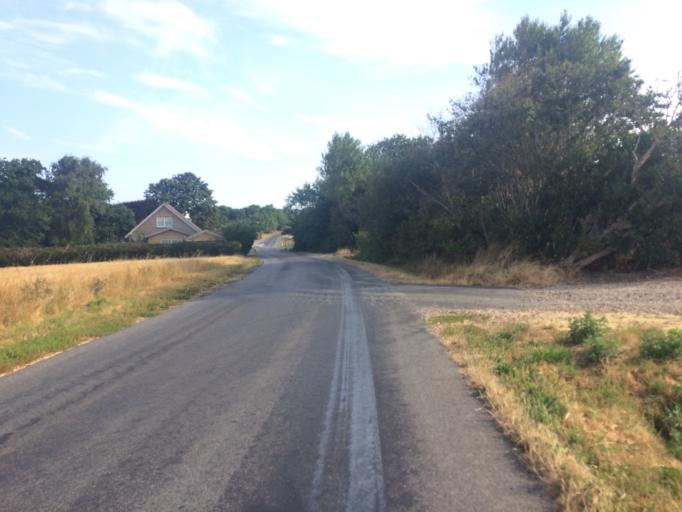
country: DK
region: Central Jutland
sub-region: Holstebro Kommune
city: Vinderup
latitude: 56.5989
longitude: 8.7595
